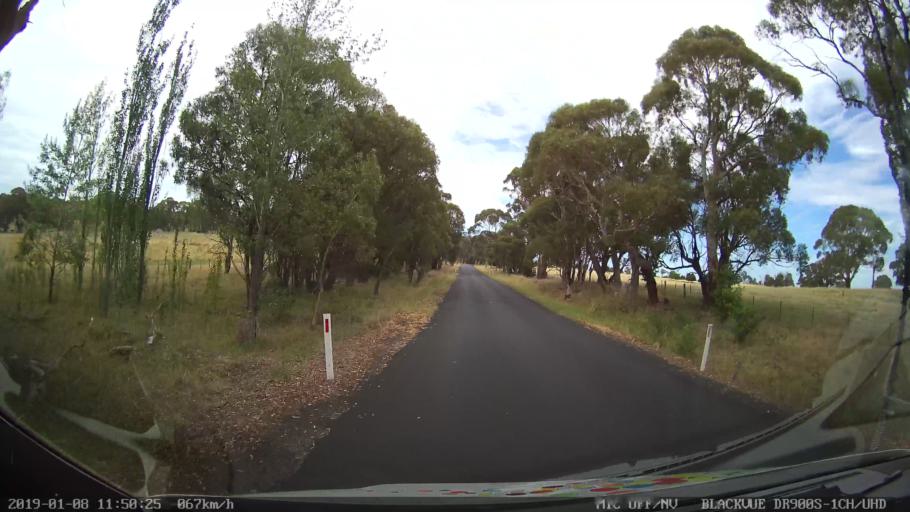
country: AU
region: New South Wales
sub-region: Armidale Dumaresq
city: Armidale
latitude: -30.3825
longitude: 151.5573
